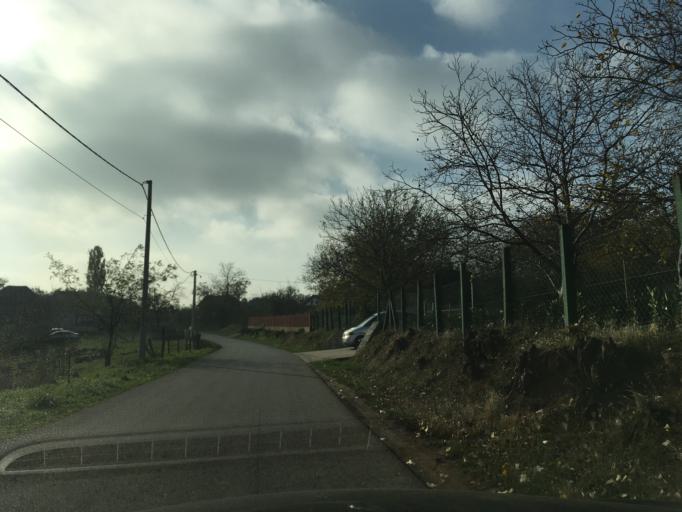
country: RS
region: Central Serbia
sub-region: Belgrade
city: Sopot
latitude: 44.4868
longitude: 20.5639
